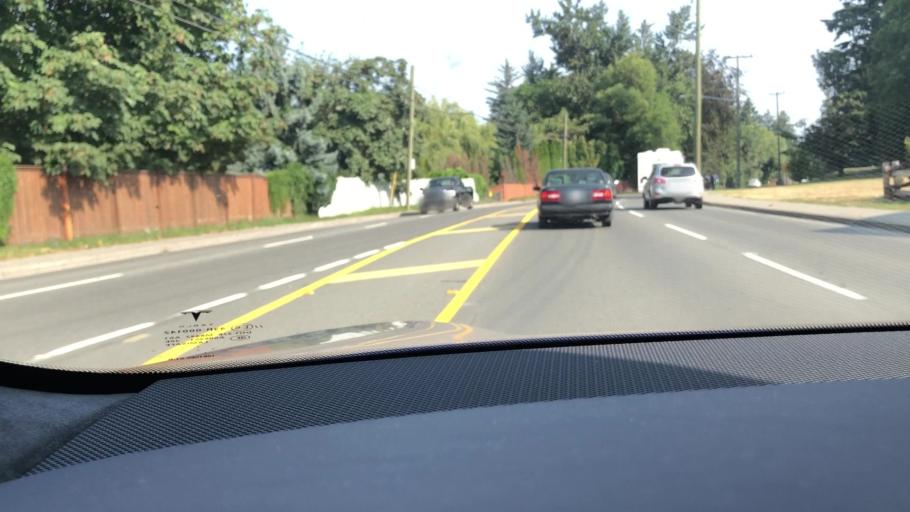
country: CA
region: British Columbia
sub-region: Fraser Valley Regional District
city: Chilliwack
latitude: 49.1246
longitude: -121.9603
